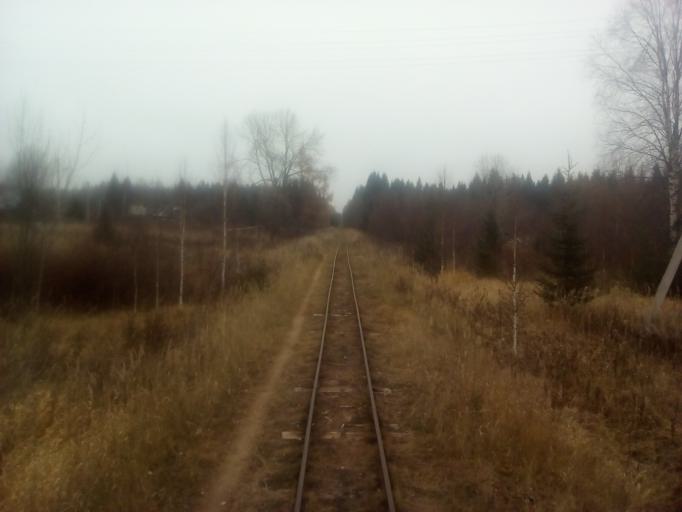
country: RU
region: Vologda
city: Kharovsk
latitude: 59.8092
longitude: 40.2614
